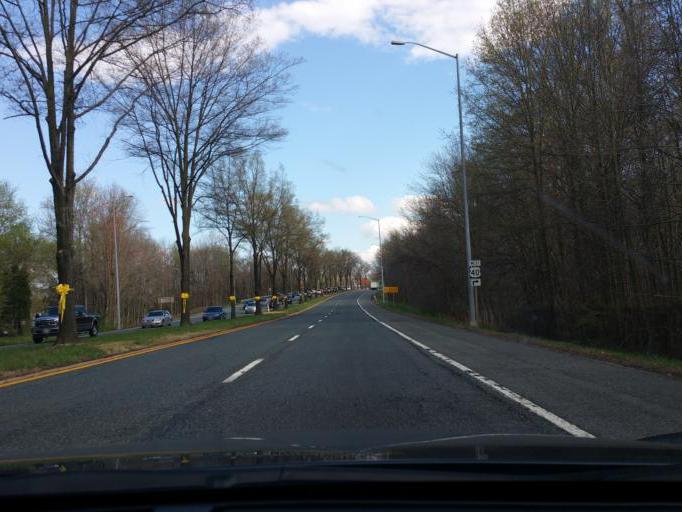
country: US
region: Maryland
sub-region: Harford County
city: Aberdeen
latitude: 39.5182
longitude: -76.1620
